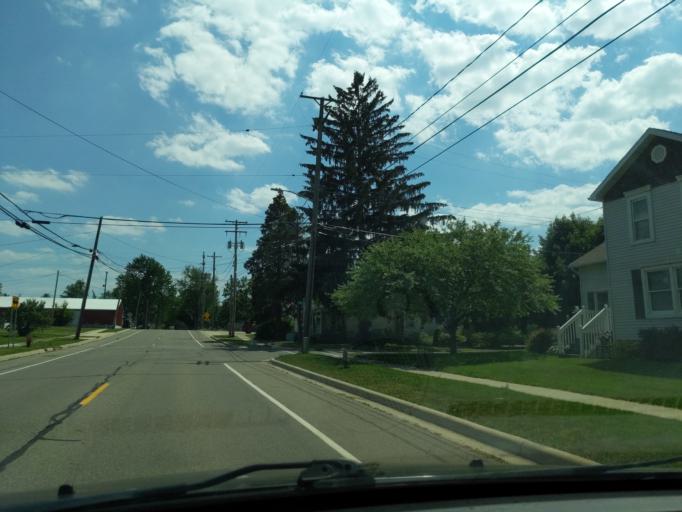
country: US
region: Michigan
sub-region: Clinton County
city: Saint Johns
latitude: 43.0058
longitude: -84.5627
